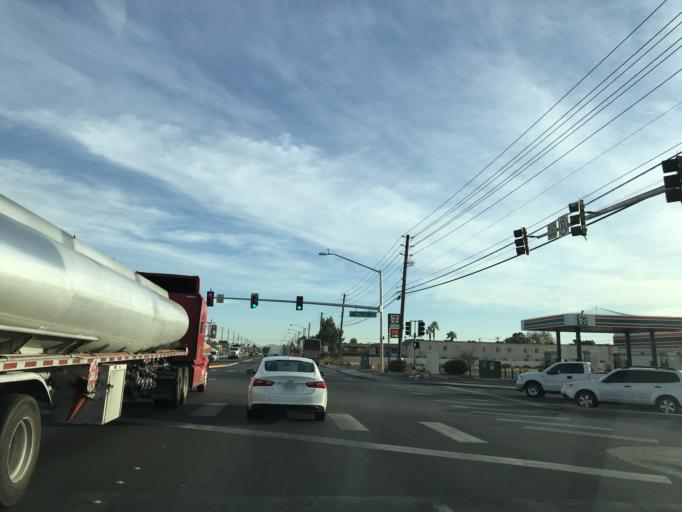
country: US
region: Nevada
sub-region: Clark County
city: Nellis Air Force Base
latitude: 36.2357
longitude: -115.0624
